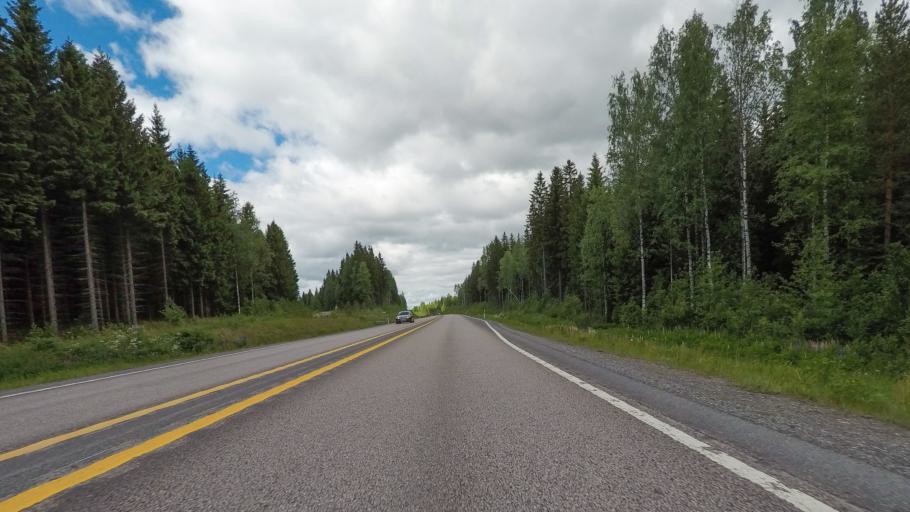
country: FI
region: Paijanne Tavastia
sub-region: Lahti
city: Hartola
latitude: 61.4317
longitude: 26.0079
